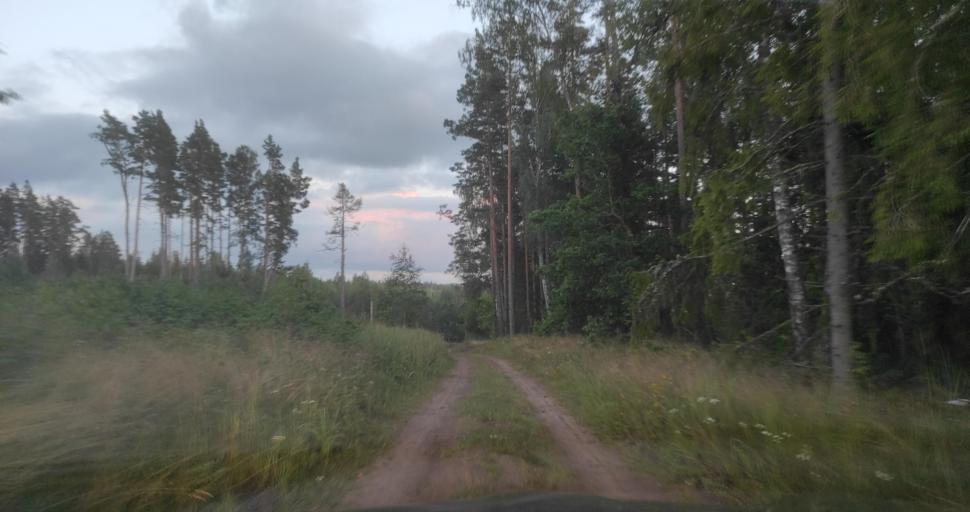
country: LV
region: Kuldigas Rajons
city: Kuldiga
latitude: 57.0653
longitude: 21.8622
